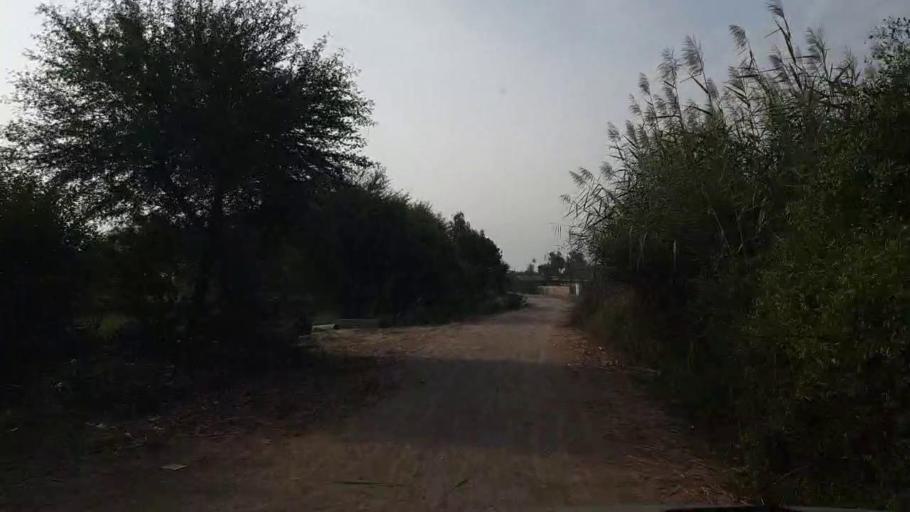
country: PK
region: Sindh
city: Rajo Khanani
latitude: 24.9121
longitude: 68.9217
